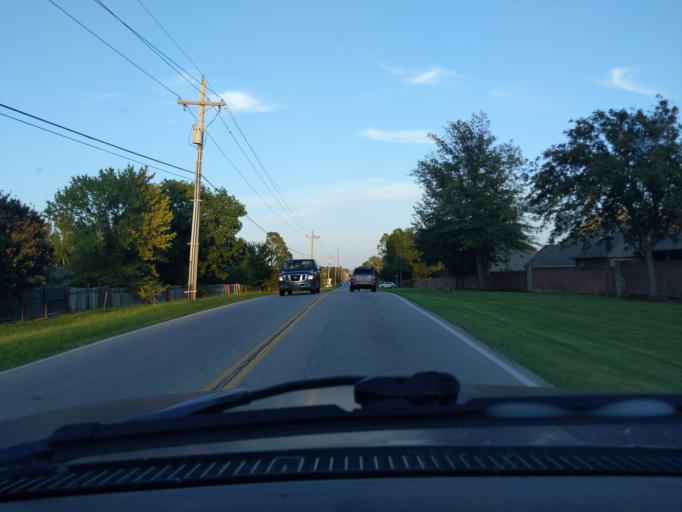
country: US
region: Oklahoma
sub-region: Tulsa County
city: Jenks
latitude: 36.0464
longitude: -95.8987
